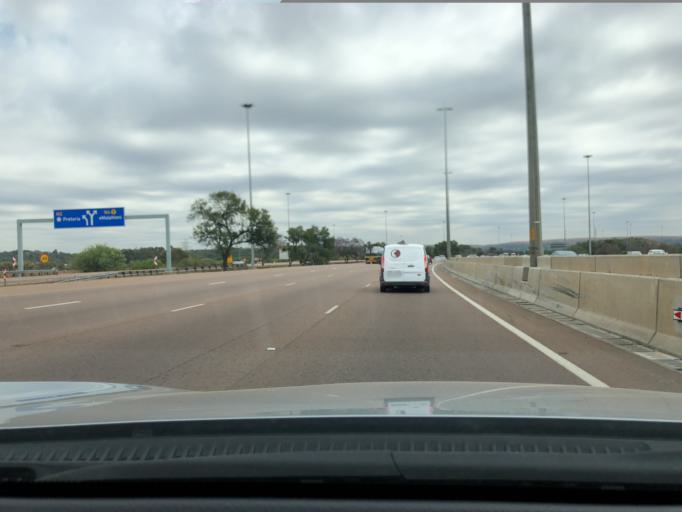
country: ZA
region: Gauteng
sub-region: City of Tshwane Metropolitan Municipality
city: Pretoria
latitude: -25.7447
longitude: 28.2671
